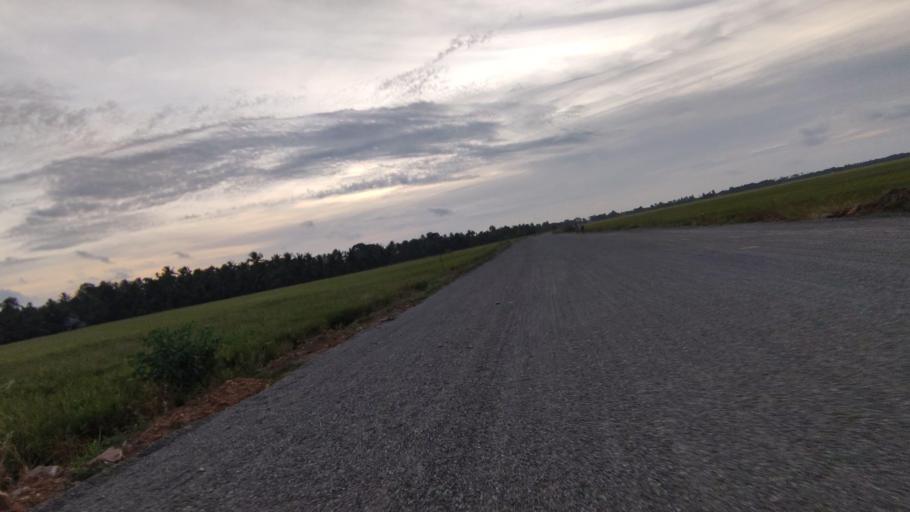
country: IN
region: Kerala
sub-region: Kottayam
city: Kottayam
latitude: 9.6474
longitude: 76.4765
